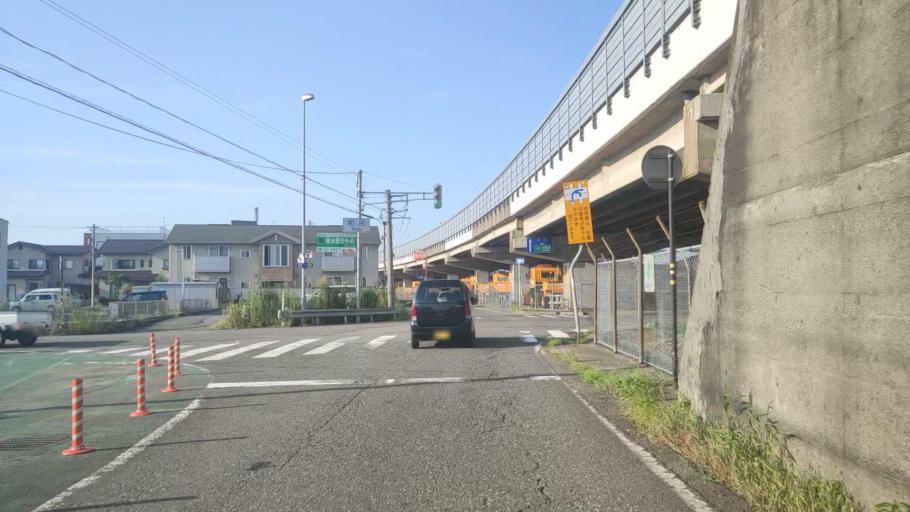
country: JP
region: Fukui
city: Fukui-shi
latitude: 36.0494
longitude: 136.2411
